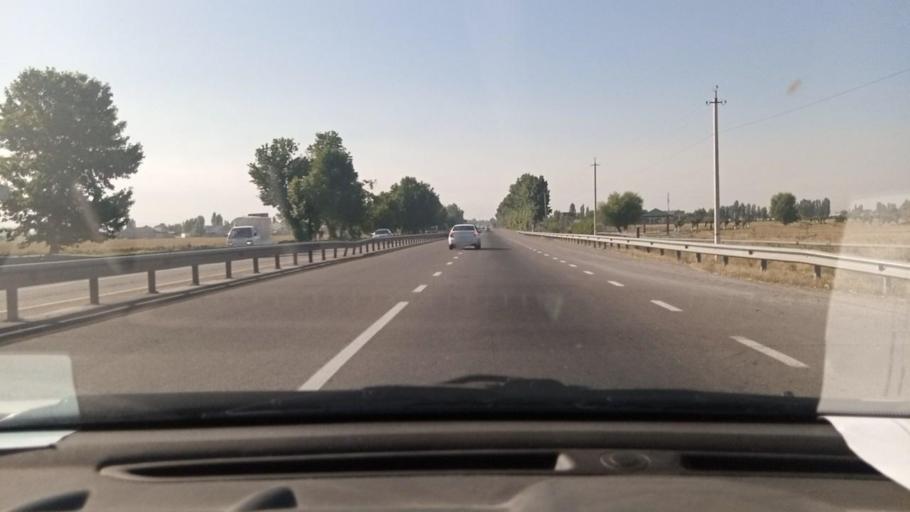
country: UZ
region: Toshkent Shahri
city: Bektemir
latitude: 41.1597
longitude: 69.4212
